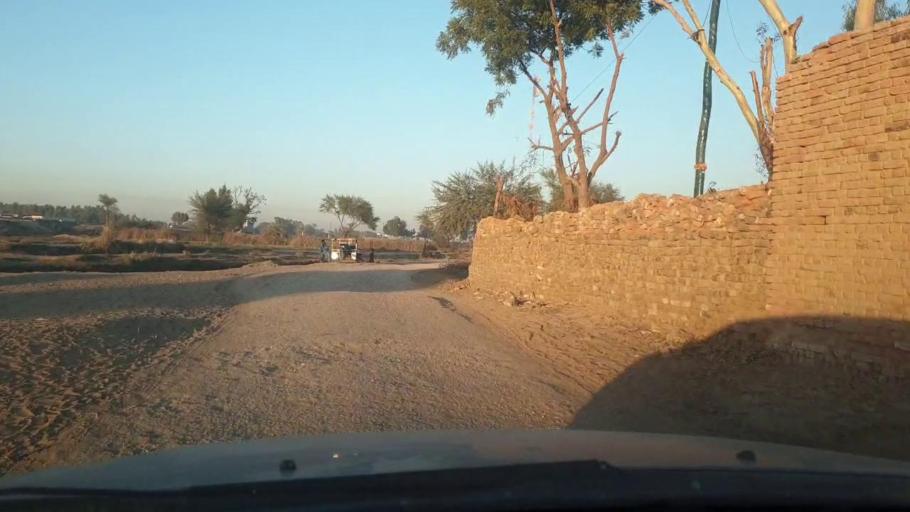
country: PK
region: Sindh
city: Pano Aqil
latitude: 27.9183
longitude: 69.1954
